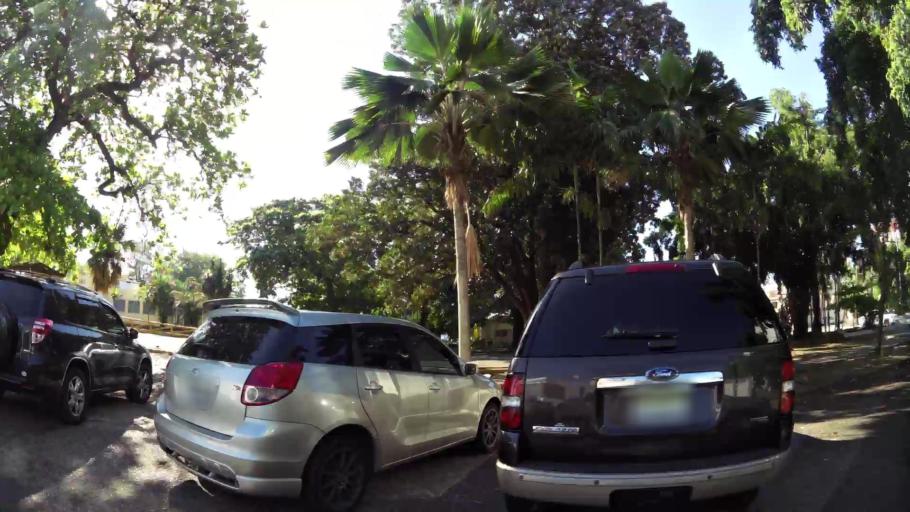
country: DO
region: Nacional
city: Ciudad Nueva
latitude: 18.4663
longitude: -69.8949
